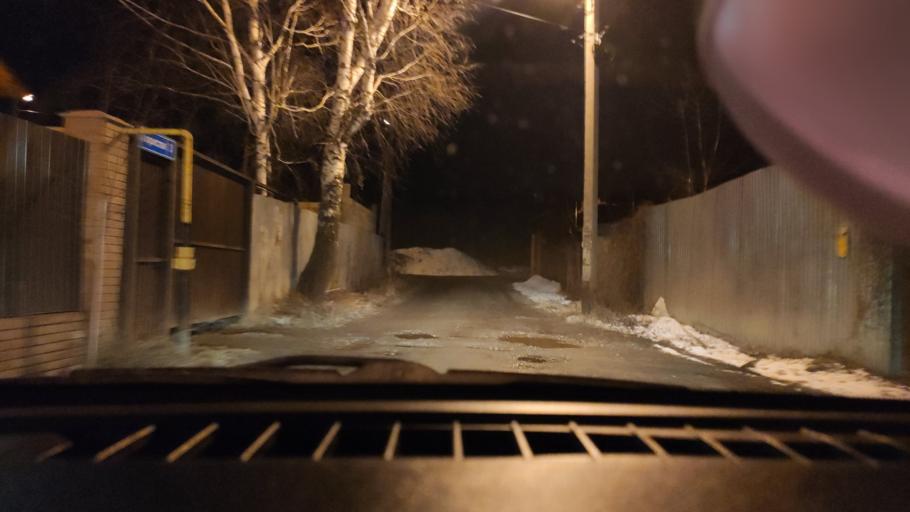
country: RU
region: Samara
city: Samara
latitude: 53.2676
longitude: 50.2329
